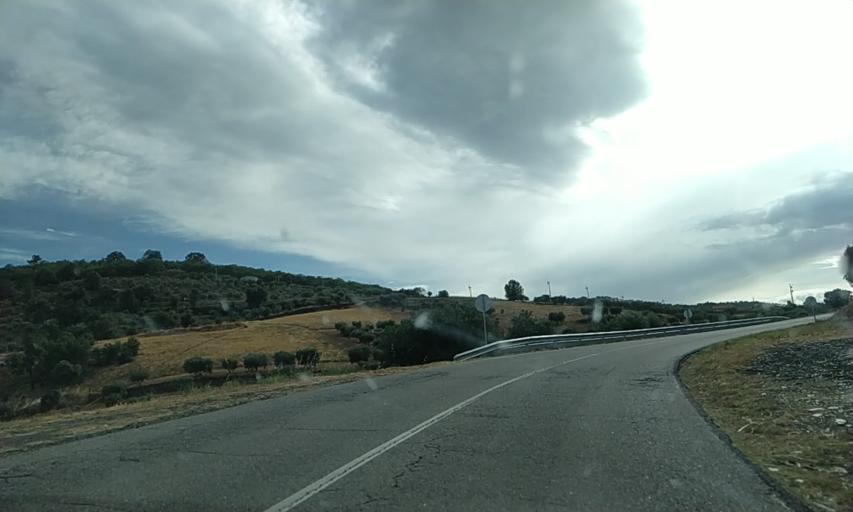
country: PT
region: Viseu
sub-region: Penedono
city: Penedono
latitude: 41.0668
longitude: -7.3983
